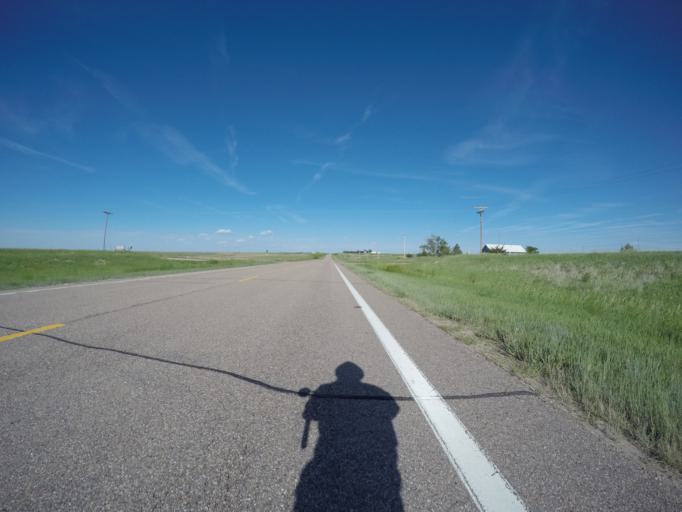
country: US
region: Kansas
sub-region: Cheyenne County
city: Saint Francis
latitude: 39.7566
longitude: -102.0318
